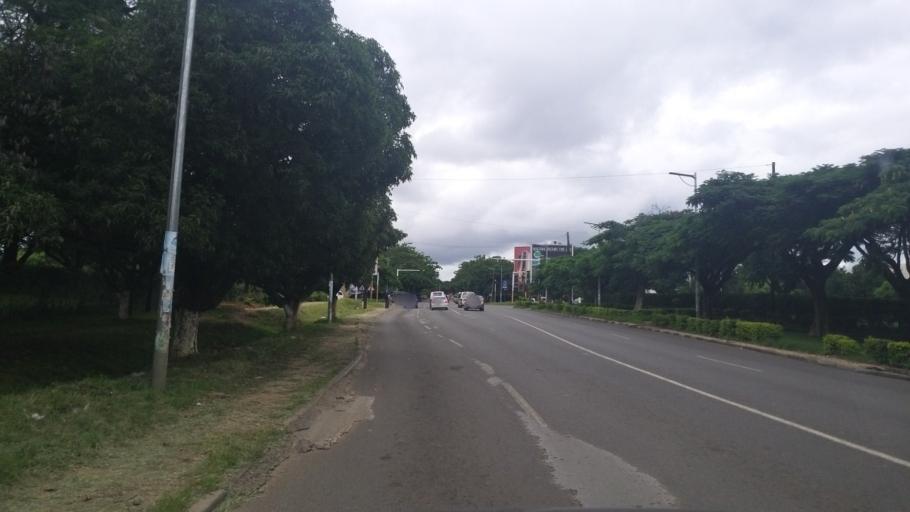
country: ZM
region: Lusaka
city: Lusaka
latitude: -15.4200
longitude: 28.3019
